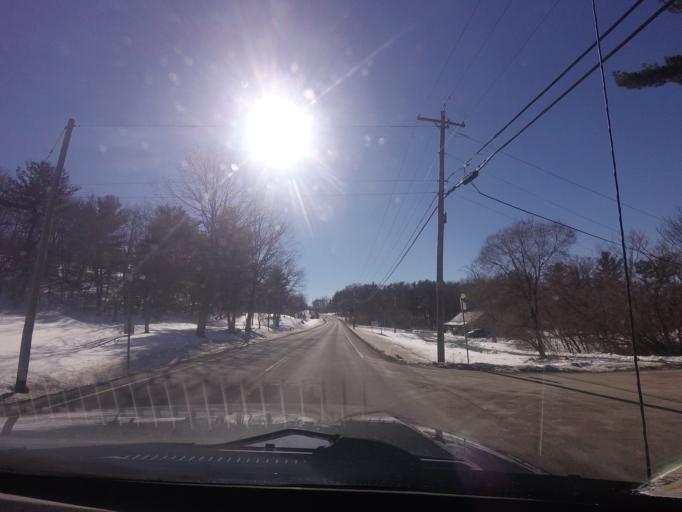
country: US
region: New York
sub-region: Saratoga County
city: Waterford
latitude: 42.8195
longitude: -73.6317
